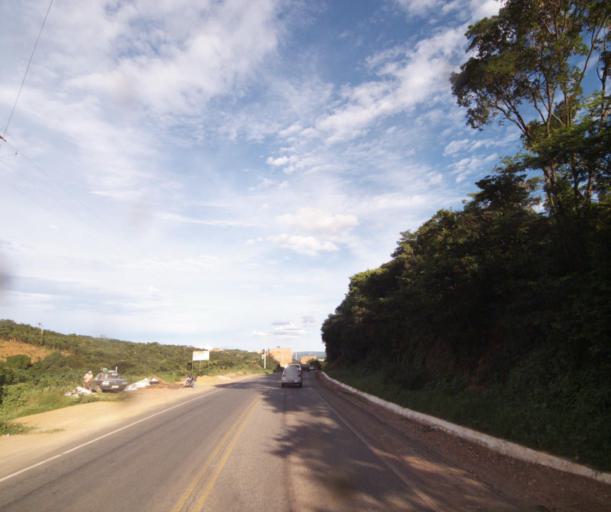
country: BR
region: Bahia
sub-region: Caetite
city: Caetite
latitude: -14.0617
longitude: -42.5021
